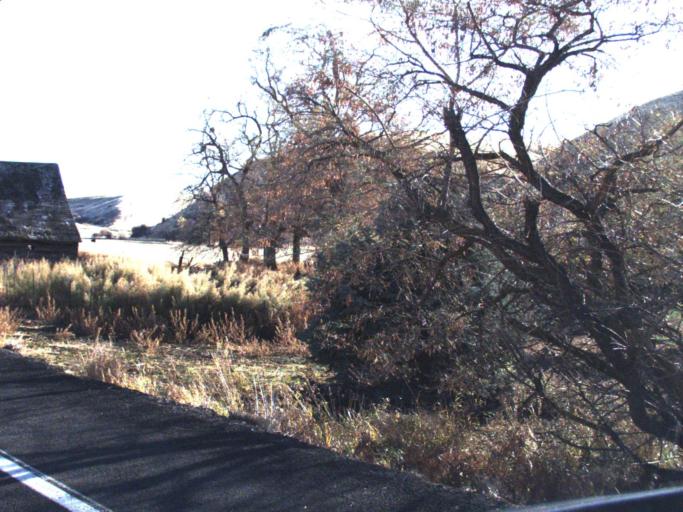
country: US
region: Washington
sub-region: Garfield County
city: Pomeroy
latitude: 46.4675
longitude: -117.4922
